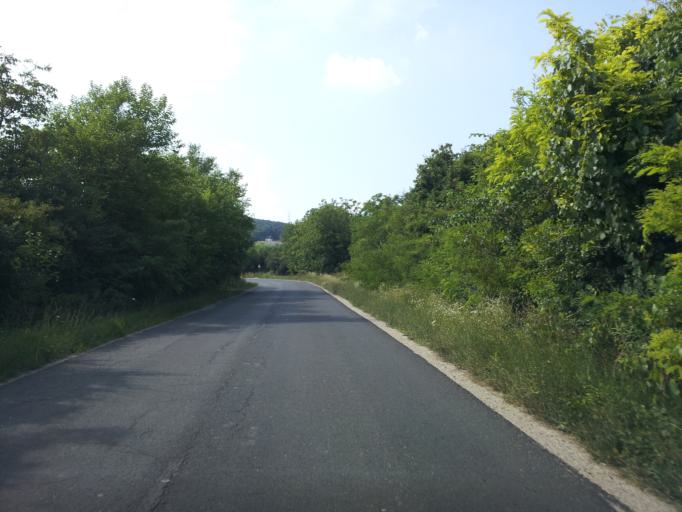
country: HU
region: Veszprem
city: Balatonfured
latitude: 46.9808
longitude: 17.8219
